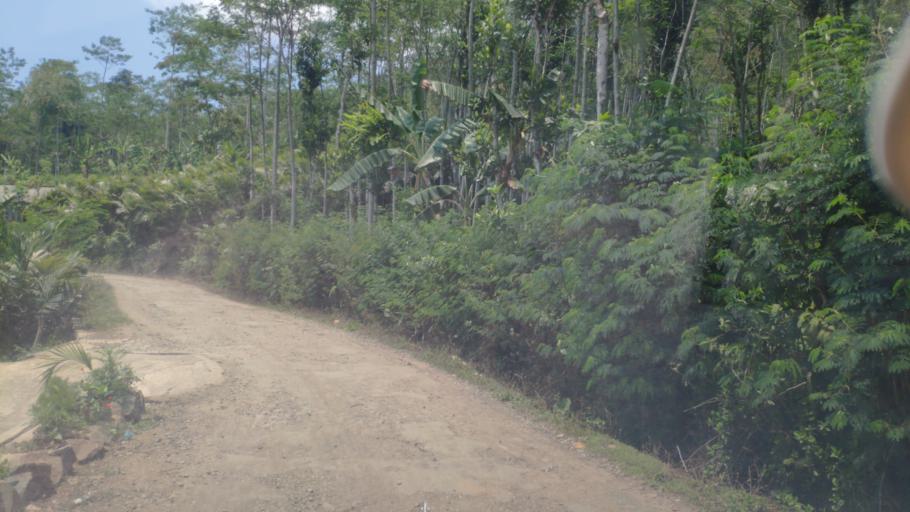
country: ID
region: Central Java
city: Wonosobo
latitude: -7.2886
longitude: 109.7357
